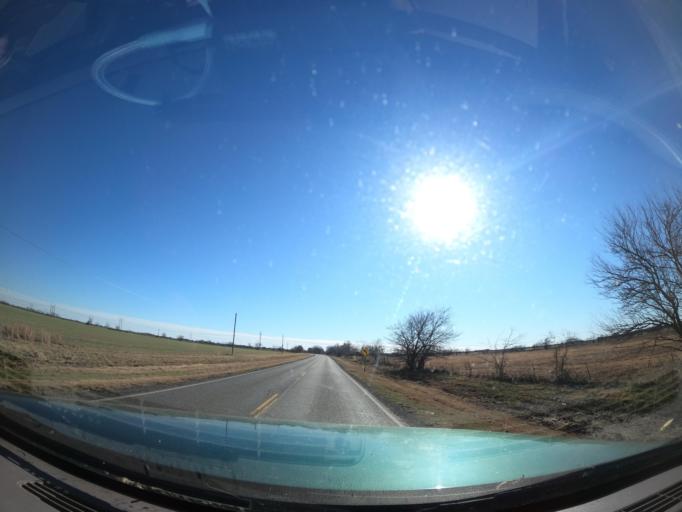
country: US
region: Oklahoma
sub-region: McIntosh County
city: Checotah
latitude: 35.5805
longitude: -95.6599
